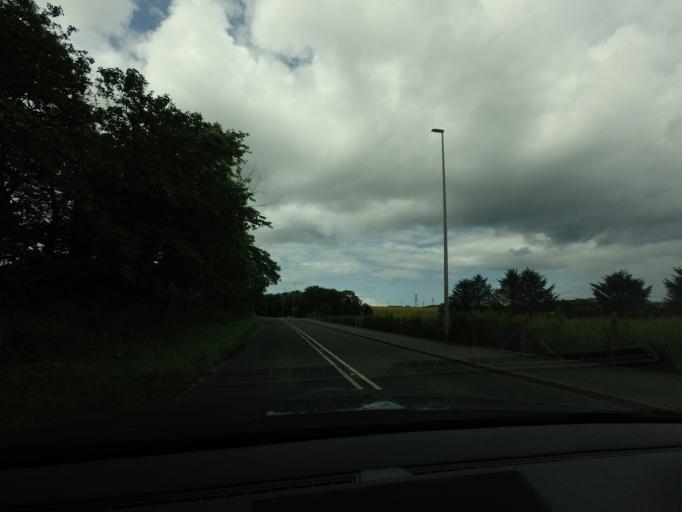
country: GB
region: Scotland
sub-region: Aberdeenshire
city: Macduff
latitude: 57.6605
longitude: -2.4934
